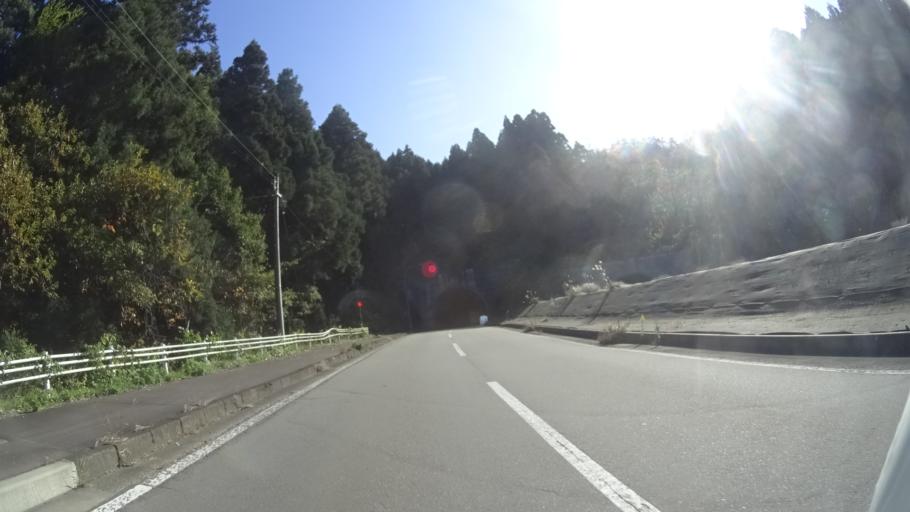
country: JP
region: Fukui
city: Ono
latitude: 35.9828
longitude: 136.4788
